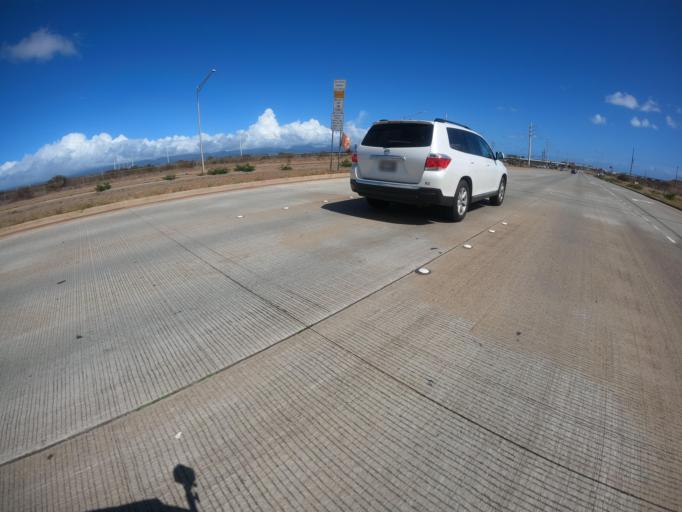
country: US
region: Hawaii
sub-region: Honolulu County
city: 'Ewa Villages
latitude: 21.3633
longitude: -158.0570
